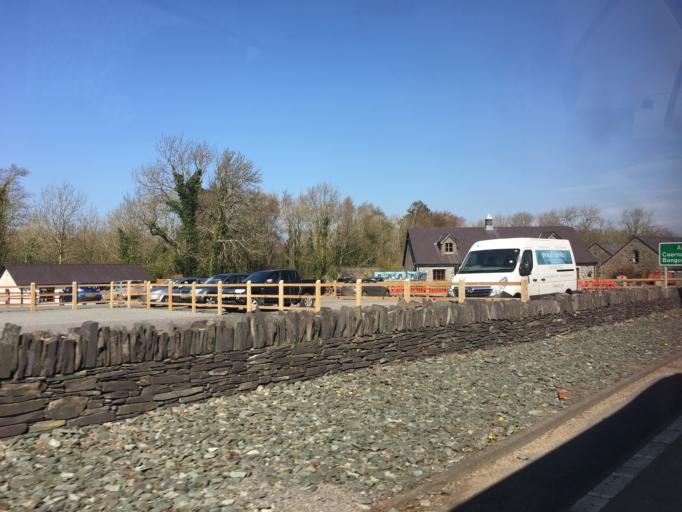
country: GB
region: Wales
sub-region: Gwynedd
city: Llanwnda
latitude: 53.0706
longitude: -4.2834
